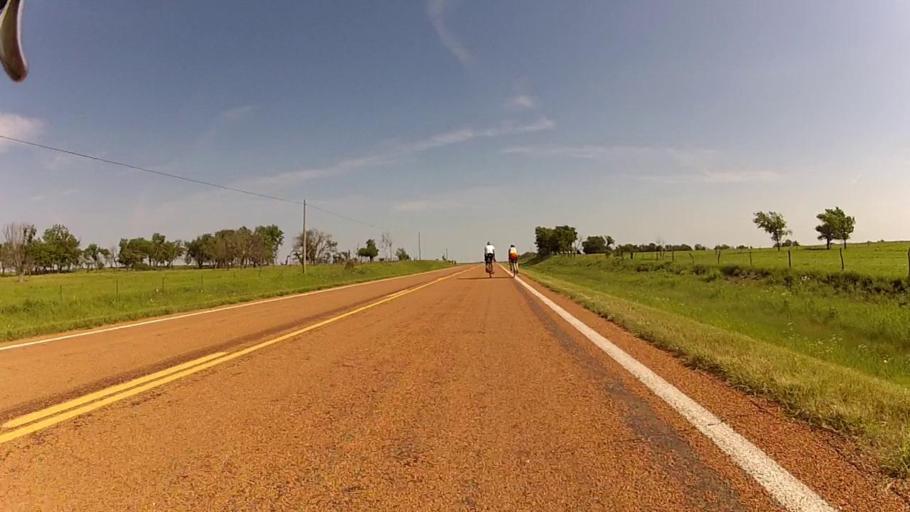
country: US
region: Kansas
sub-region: Cowley County
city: Winfield
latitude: 37.0816
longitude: -96.6436
